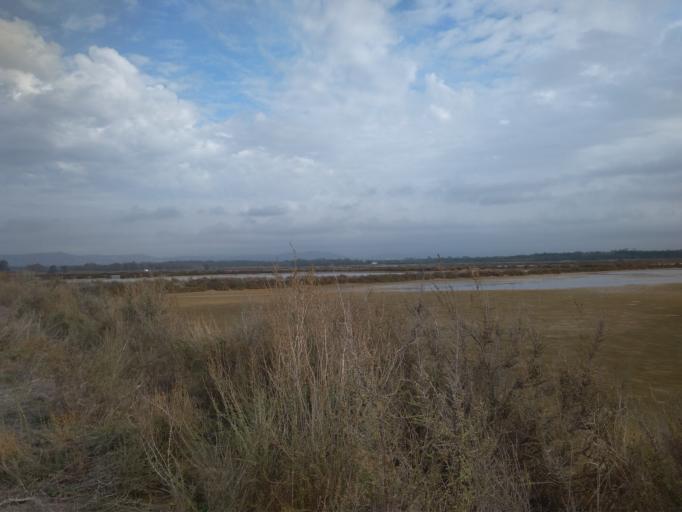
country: PT
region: Faro
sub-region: Faro
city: Faro
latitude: 37.0212
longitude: -7.9970
